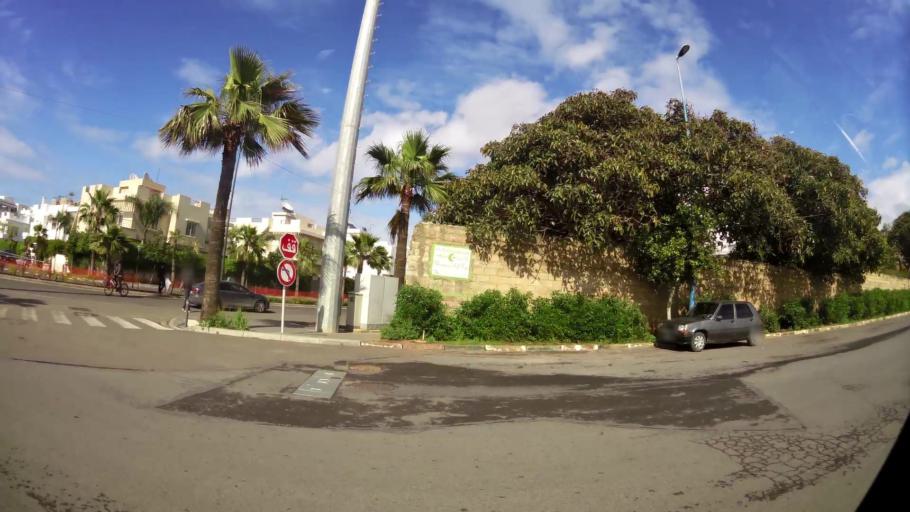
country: MA
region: Grand Casablanca
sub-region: Casablanca
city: Casablanca
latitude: 33.5700
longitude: -7.6974
